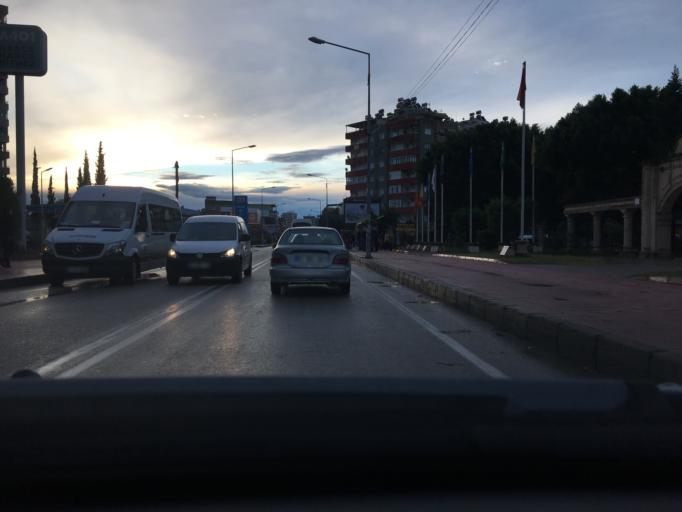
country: TR
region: Adana
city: Seyhan
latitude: 37.0211
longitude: 35.2942
